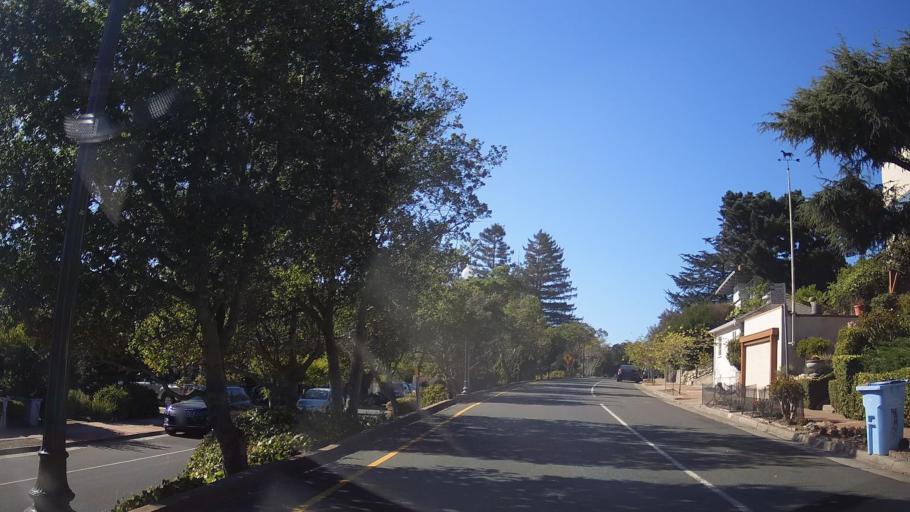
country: US
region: California
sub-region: Alameda County
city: Berkeley
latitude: 37.8914
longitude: -122.2732
